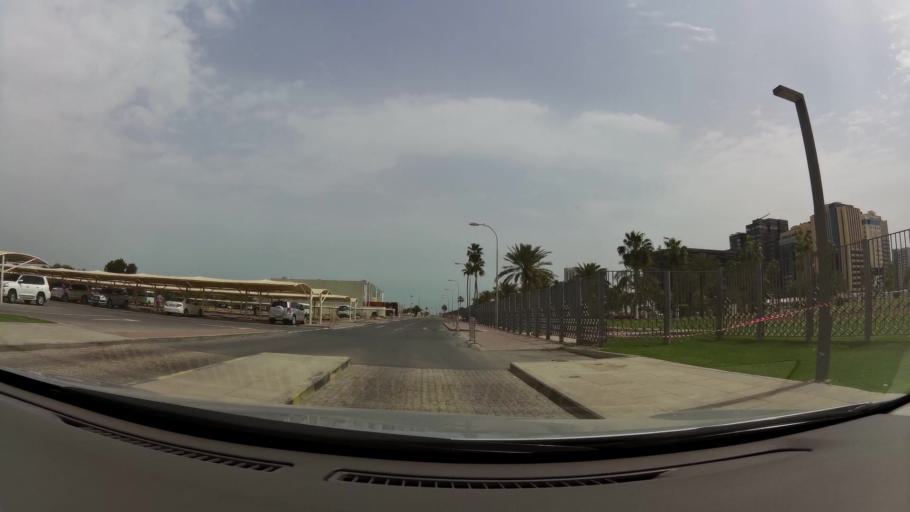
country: QA
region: Baladiyat ad Dawhah
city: Doha
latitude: 25.2927
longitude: 51.5407
